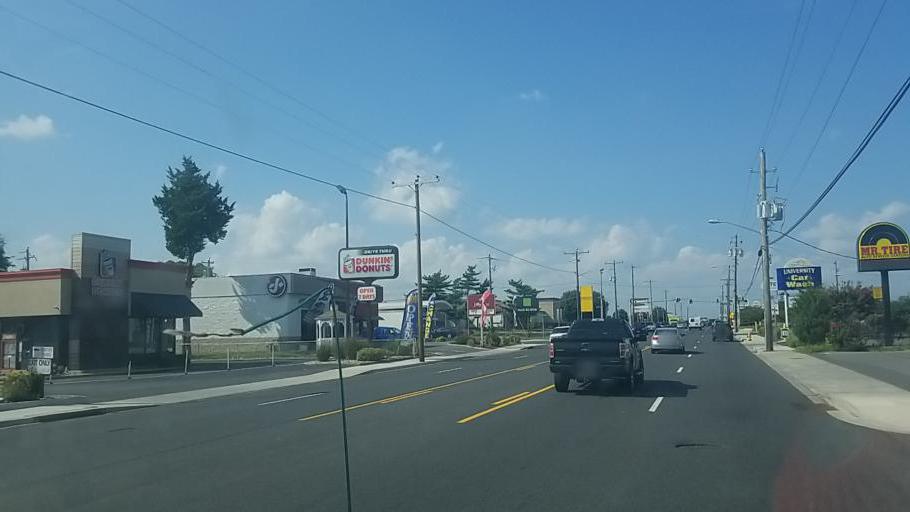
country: US
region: Maryland
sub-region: Wicomico County
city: Salisbury
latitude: 38.3521
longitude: -75.6013
